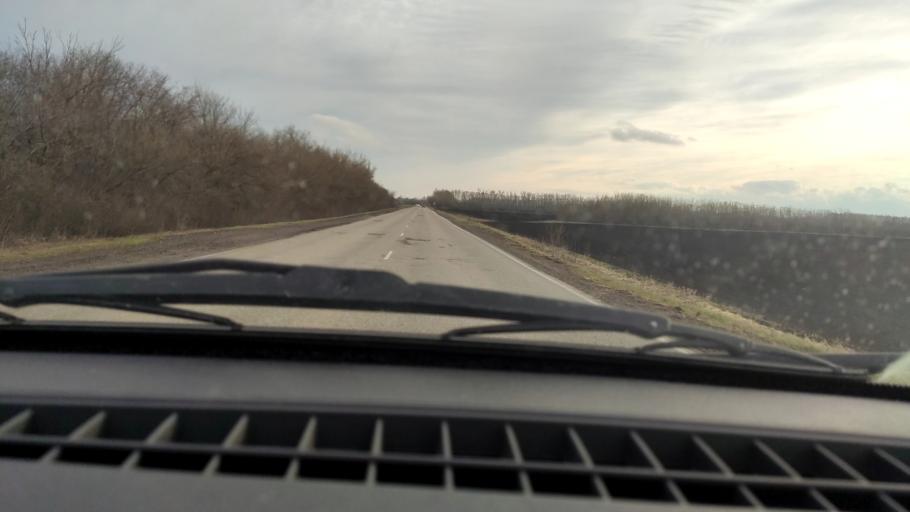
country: RU
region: Bashkortostan
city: Chishmy
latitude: 54.4610
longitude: 55.2550
